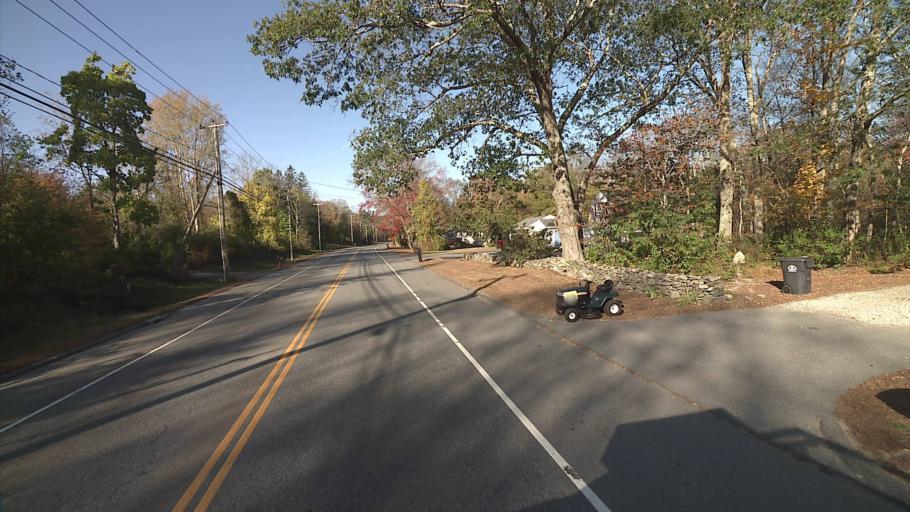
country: US
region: Connecticut
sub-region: Windham County
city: Wauregan
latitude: 41.7825
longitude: -71.9816
